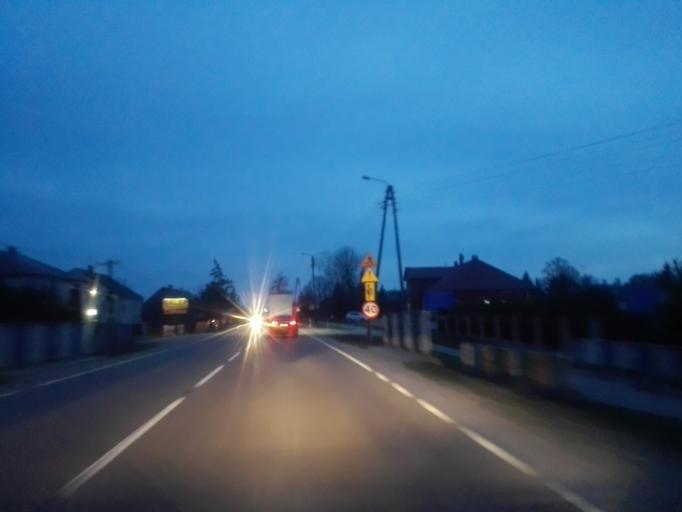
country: PL
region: Podlasie
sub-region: Lomza
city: Lomza
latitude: 53.1346
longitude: 22.0418
